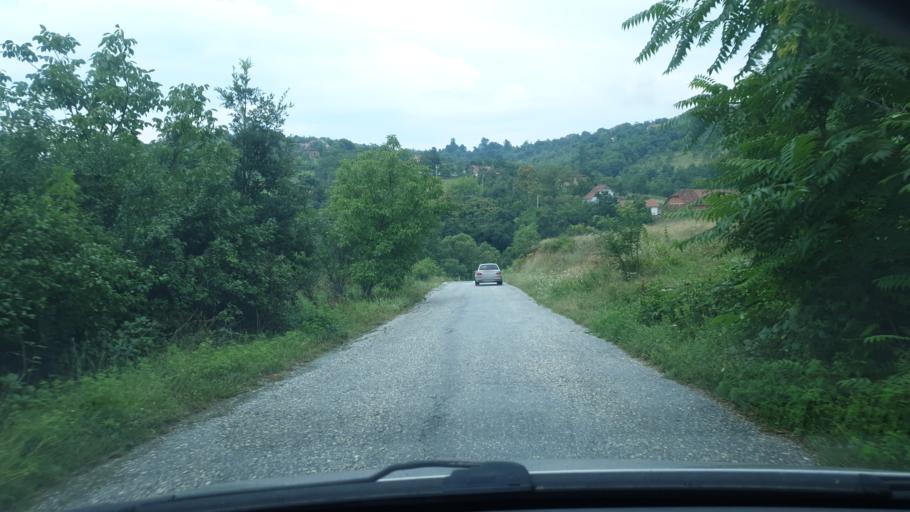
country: RS
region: Central Serbia
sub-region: Sumadijski Okrug
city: Kragujevac
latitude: 44.0714
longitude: 20.7874
